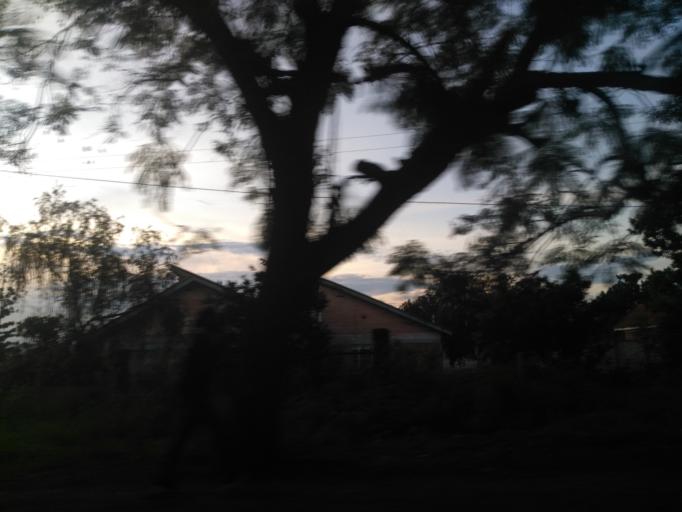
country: UG
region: Eastern Region
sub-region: Jinja District
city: Jinja
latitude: 0.4285
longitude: 33.2035
